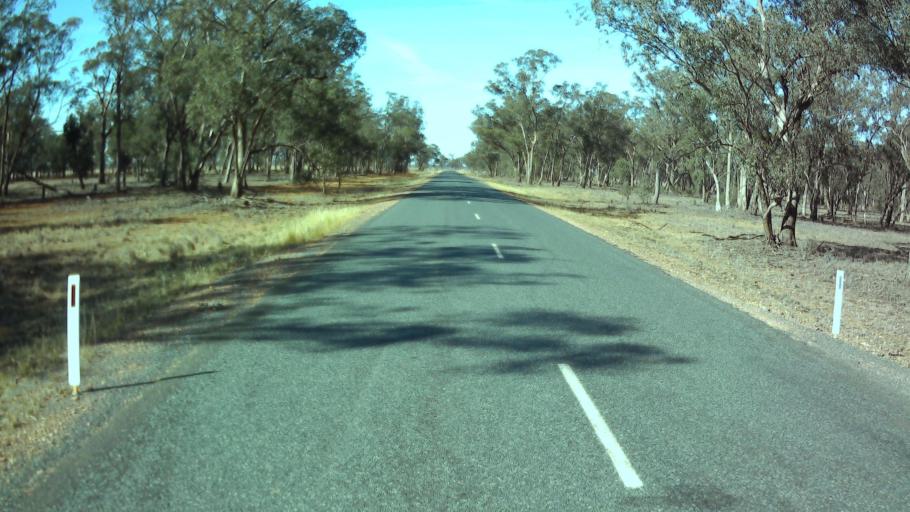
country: AU
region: New South Wales
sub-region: Weddin
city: Grenfell
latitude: -34.0648
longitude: 147.9076
